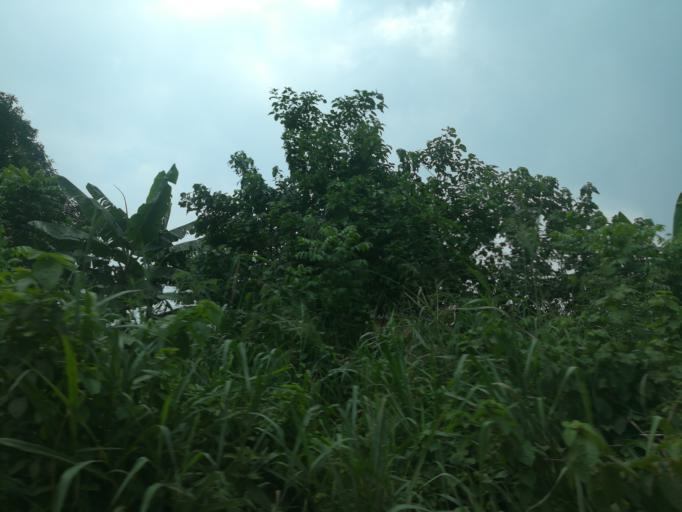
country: NG
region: Lagos
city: Ikorodu
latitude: 6.5790
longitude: 3.5901
